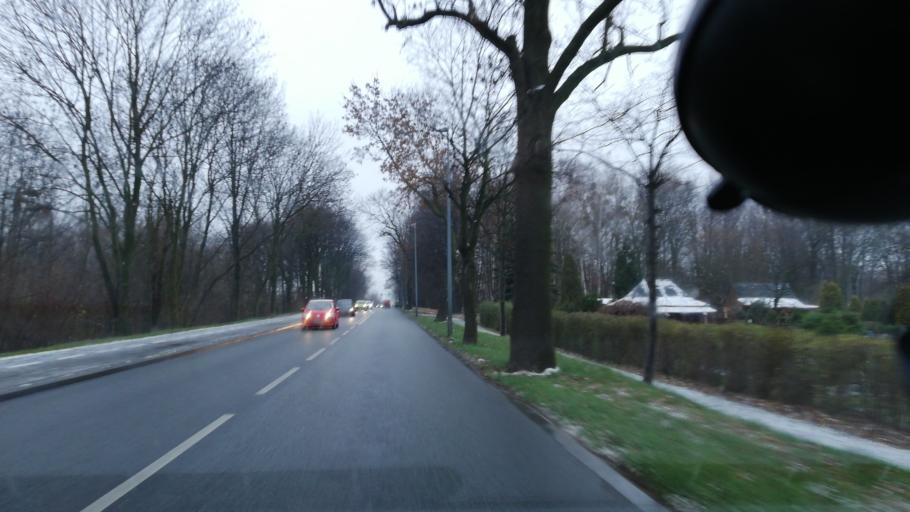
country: PL
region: Silesian Voivodeship
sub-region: Chorzow
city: Chorzow
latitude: 50.3001
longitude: 18.9852
